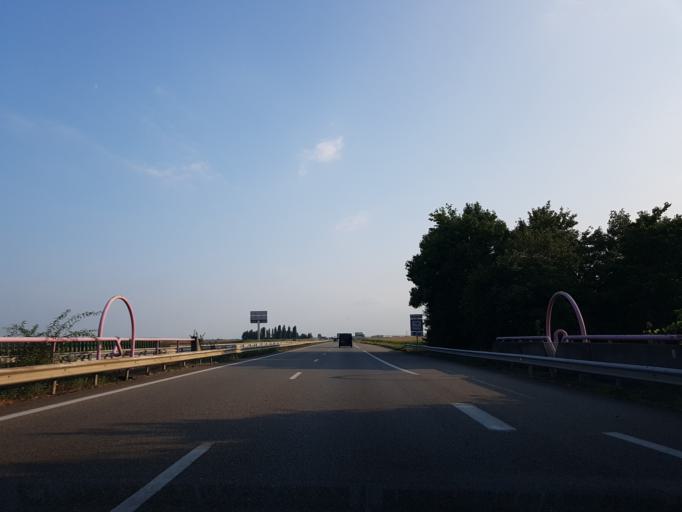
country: FR
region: Alsace
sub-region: Departement du Haut-Rhin
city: Sainte-Croix-en-Plaine
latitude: 47.9881
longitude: 7.3771
